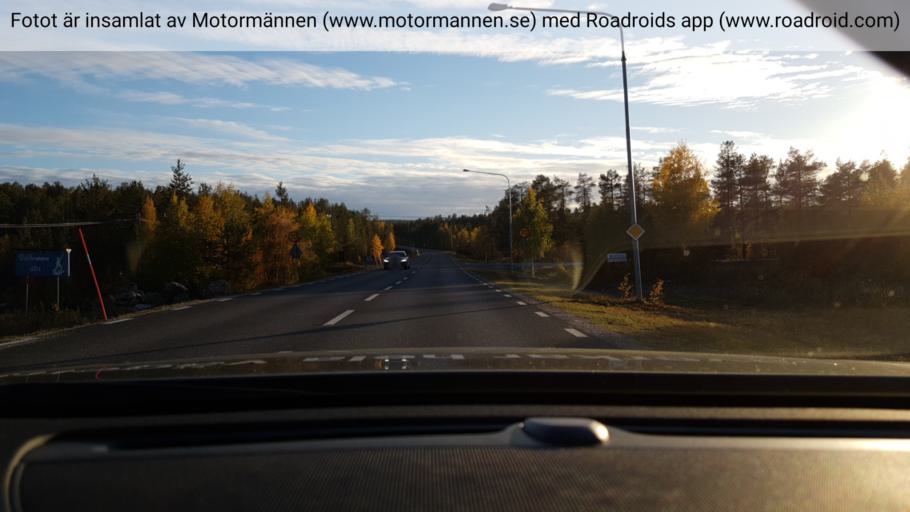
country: SE
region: Norrbotten
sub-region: Jokkmokks Kommun
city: Jokkmokk
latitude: 66.6027
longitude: 19.8191
